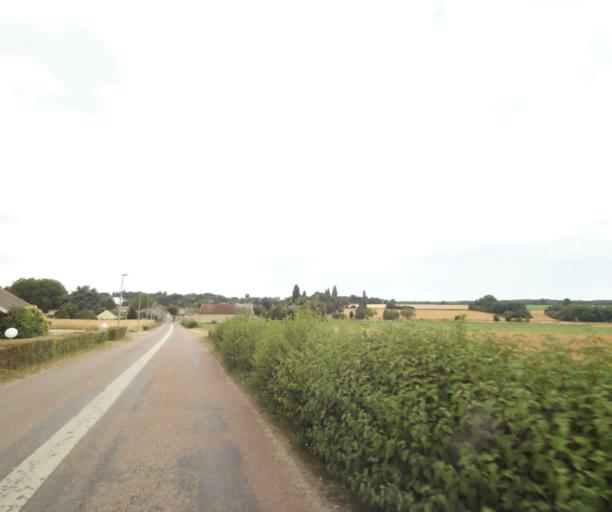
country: FR
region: Ile-de-France
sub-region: Departement de l'Essonne
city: Soisy-sur-Ecole
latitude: 48.4731
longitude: 2.5149
